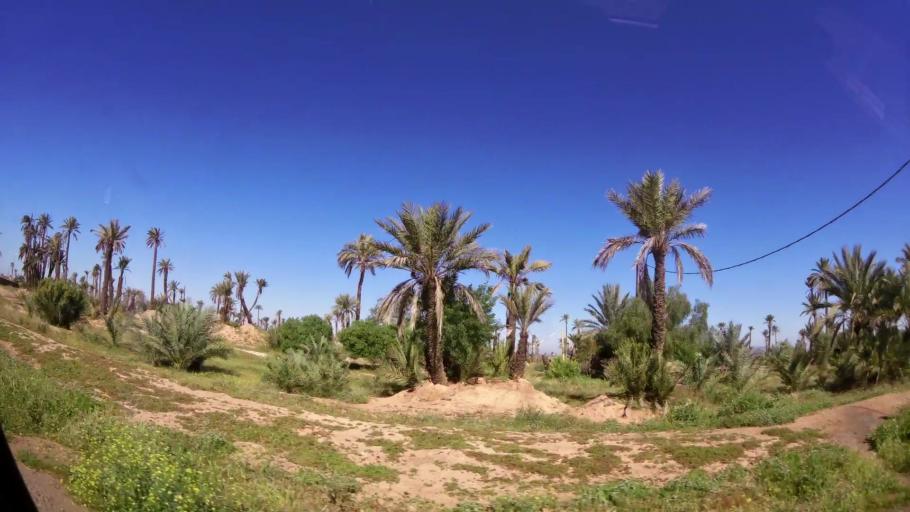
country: MA
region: Marrakech-Tensift-Al Haouz
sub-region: Marrakech
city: Marrakesh
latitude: 31.6606
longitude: -7.9471
